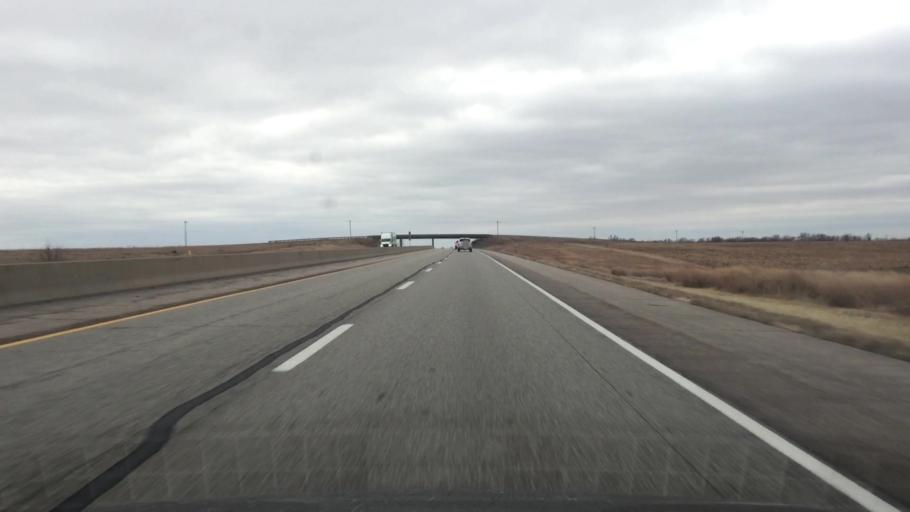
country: US
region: Kansas
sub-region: Butler County
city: El Dorado
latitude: 37.9877
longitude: -96.7045
